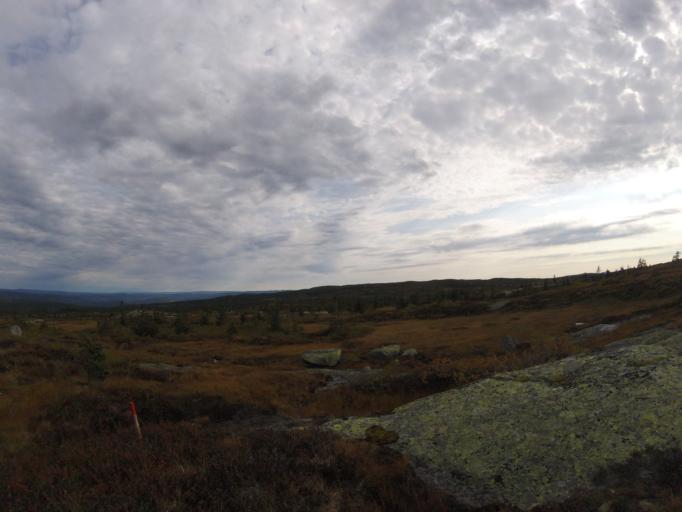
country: NO
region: Buskerud
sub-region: Rollag
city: Rollag
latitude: 59.8078
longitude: 9.3199
